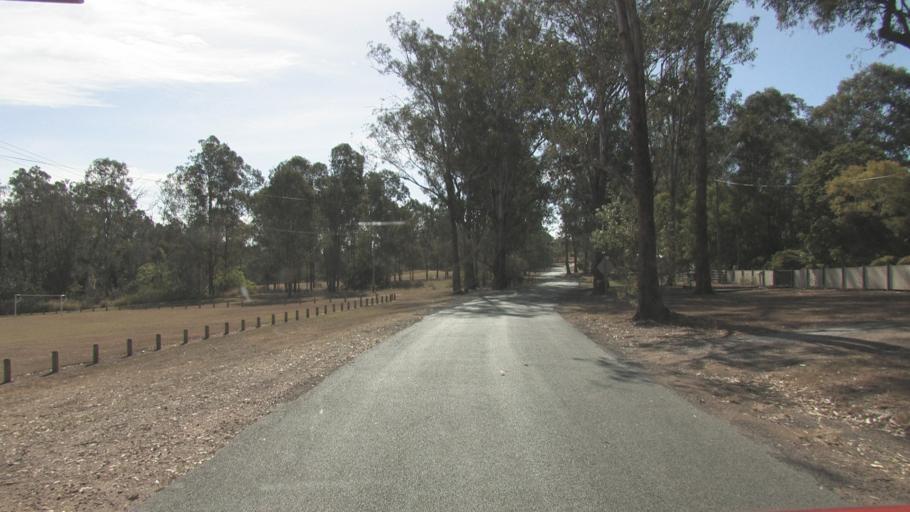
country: AU
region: Queensland
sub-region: Logan
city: Cedar Vale
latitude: -27.8593
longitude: 152.9795
